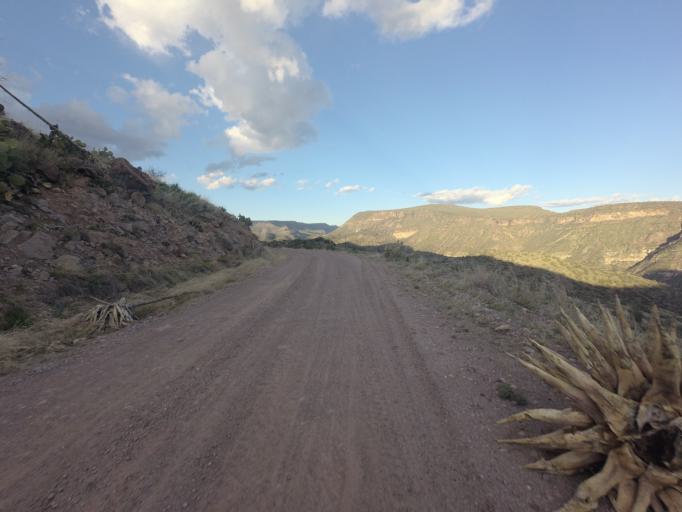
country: US
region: Arizona
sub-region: Gila County
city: Pine
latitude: 34.3612
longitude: -111.6767
